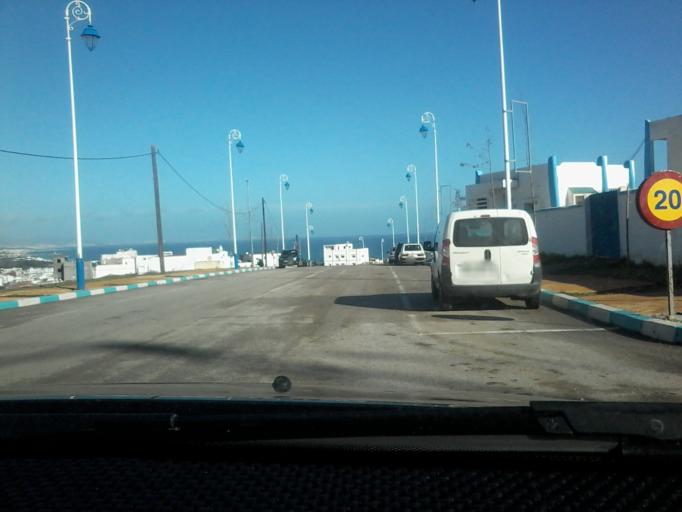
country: MA
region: Tanger-Tetouan
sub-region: Tetouan
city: Martil
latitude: 35.6759
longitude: -5.3260
